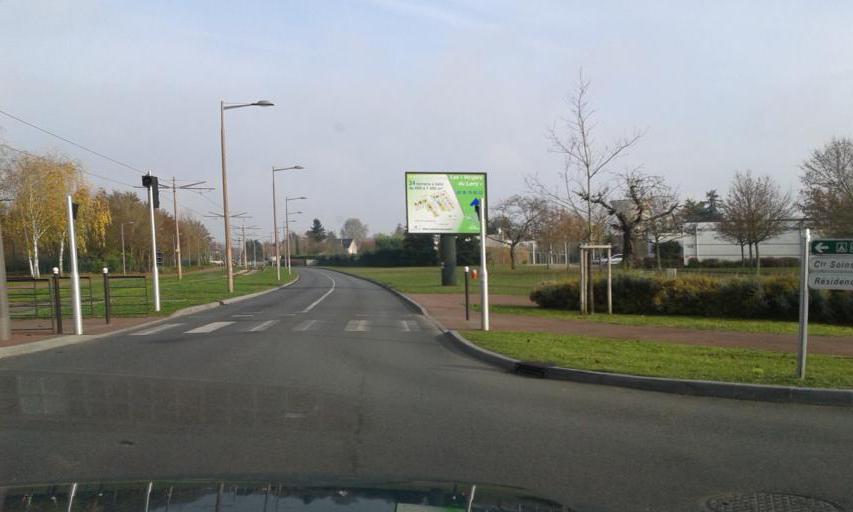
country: FR
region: Centre
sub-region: Departement du Loiret
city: Olivet
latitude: 47.8586
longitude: 1.9065
